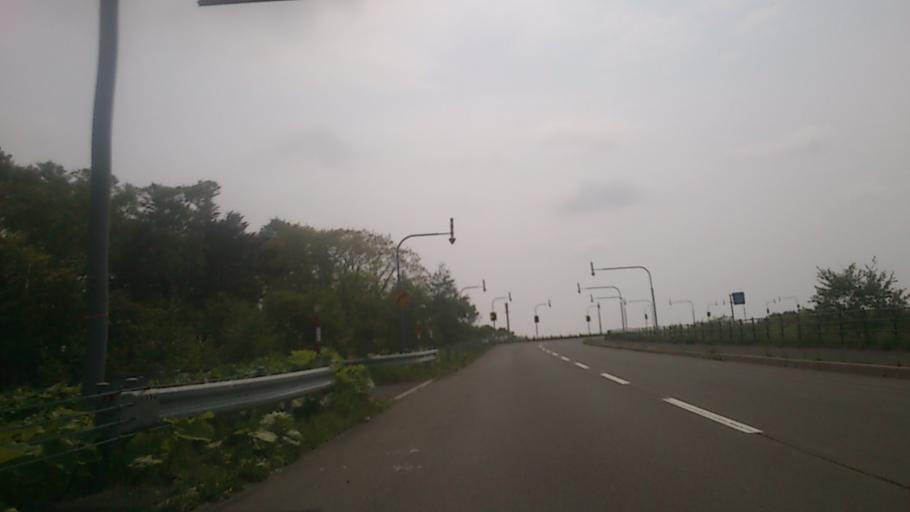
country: JP
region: Hokkaido
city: Nemuro
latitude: 43.2727
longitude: 145.5459
